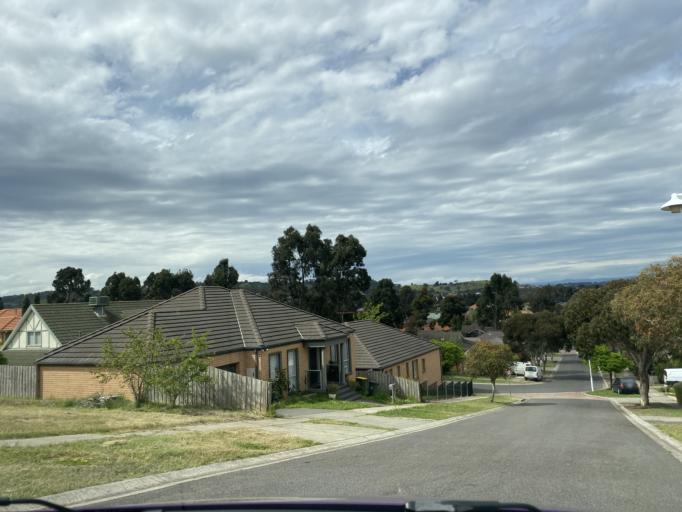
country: AU
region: Victoria
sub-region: Whittlesea
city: Mill Park
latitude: -37.6358
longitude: 145.0629
